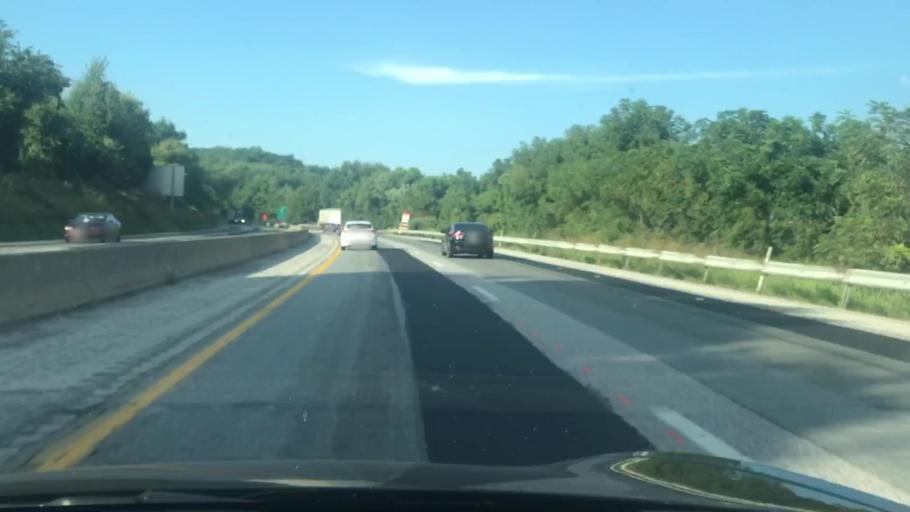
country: US
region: Pennsylvania
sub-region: York County
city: Spry
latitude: 39.9393
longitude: -76.6800
